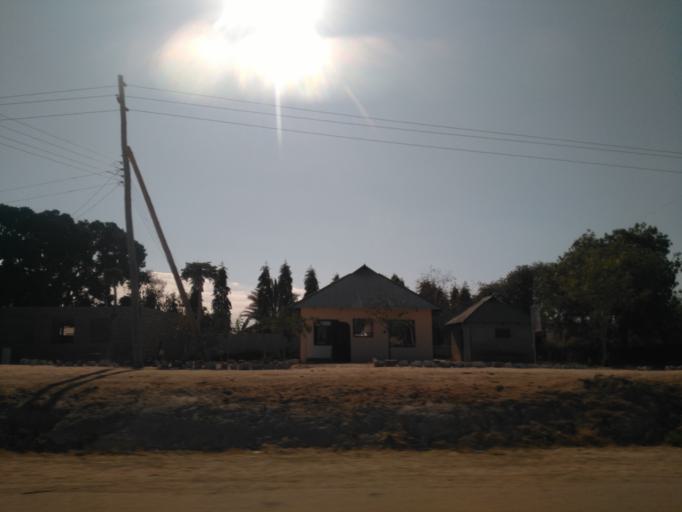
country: TZ
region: Dodoma
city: Dodoma
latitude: -6.1053
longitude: 35.7478
